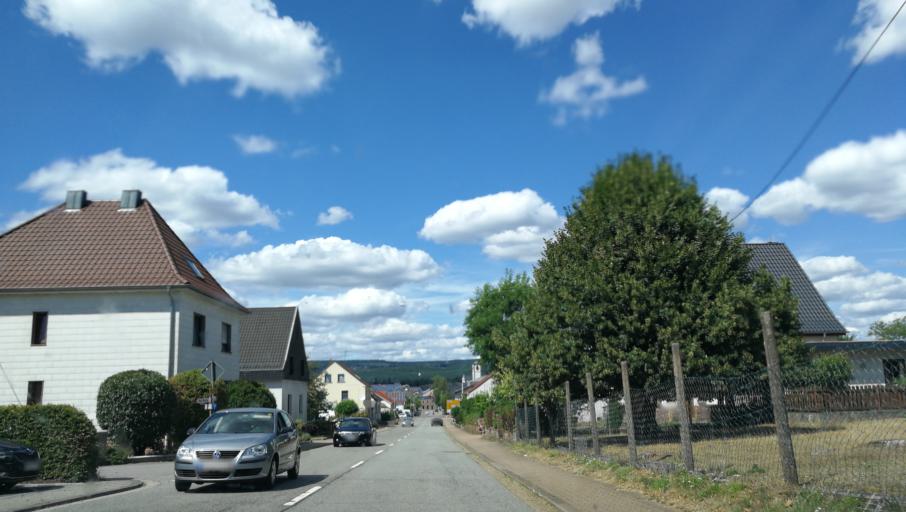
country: DE
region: Saarland
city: Losheim
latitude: 49.5037
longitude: 6.7448
